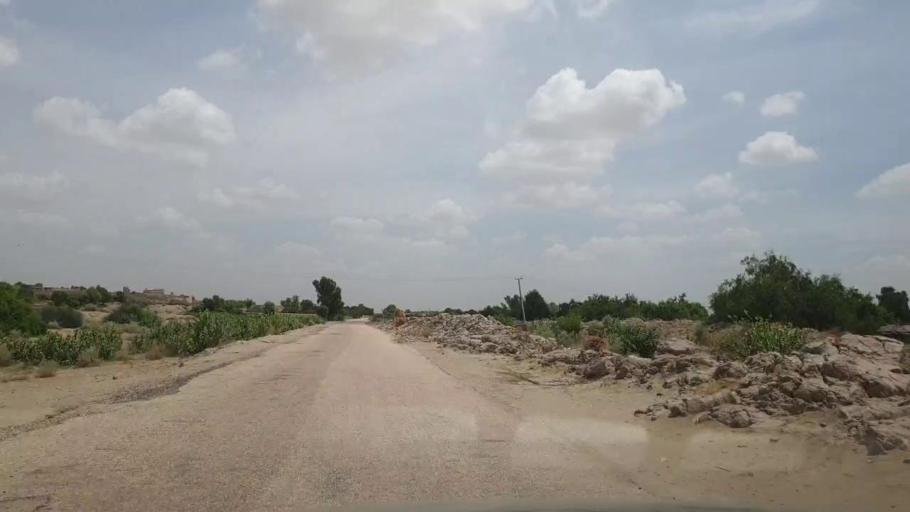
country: PK
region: Sindh
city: Kot Diji
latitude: 27.2121
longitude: 69.1136
